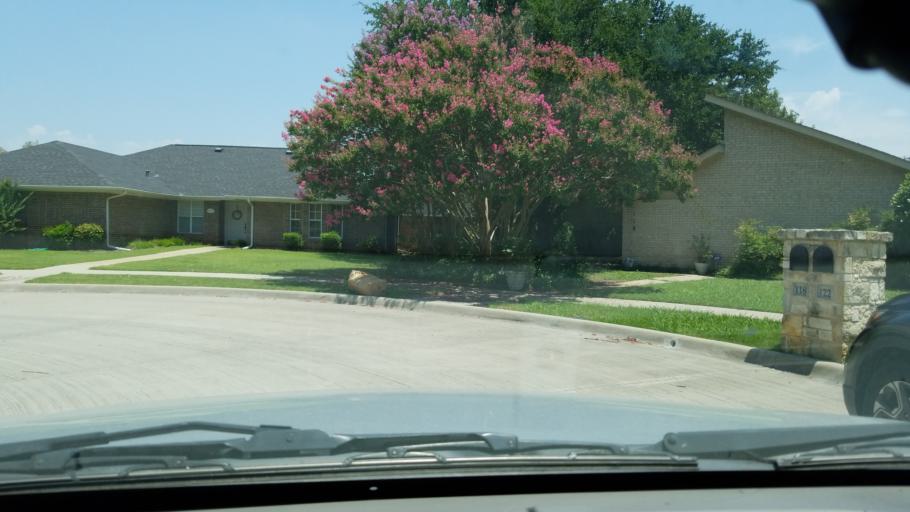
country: US
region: Texas
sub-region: Dallas County
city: Coppell
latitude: 32.9678
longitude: -96.9842
